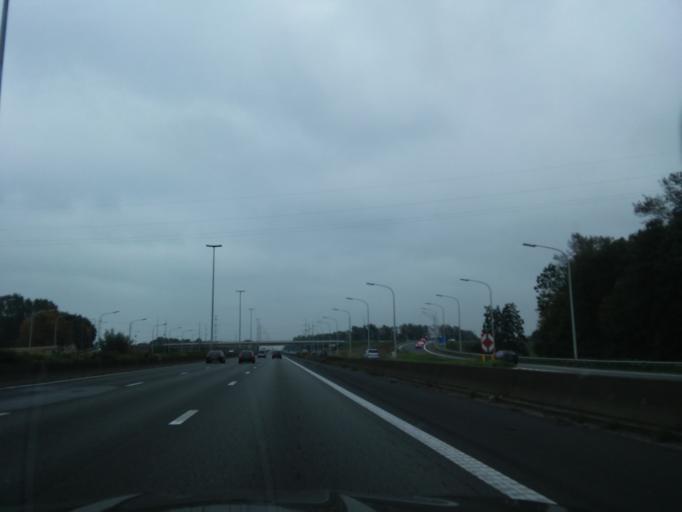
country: BE
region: Flanders
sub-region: Provincie Oost-Vlaanderen
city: Sint-Niklaas
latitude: 51.1347
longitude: 4.1386
